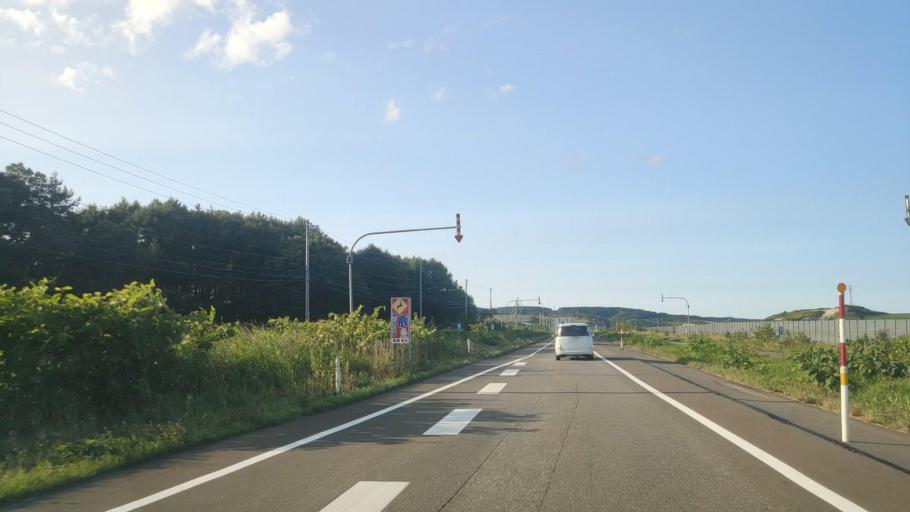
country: JP
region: Hokkaido
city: Wakkanai
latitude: 45.3243
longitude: 141.7196
